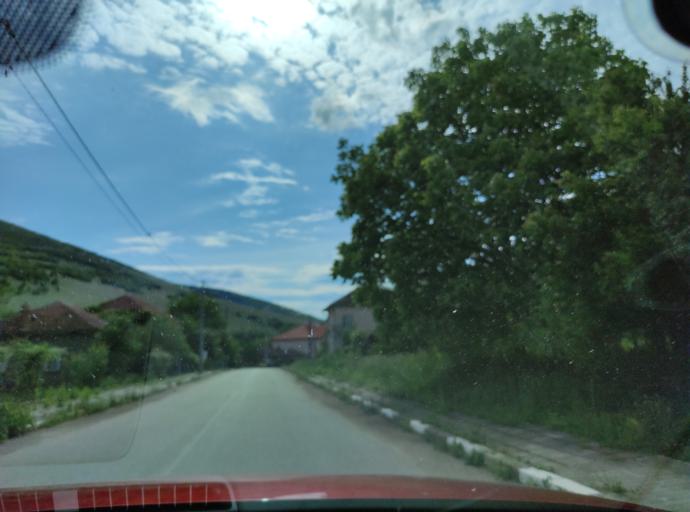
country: BG
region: Vidin
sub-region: Obshtina Belogradchik
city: Belogradchik
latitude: 43.5171
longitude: 22.7317
